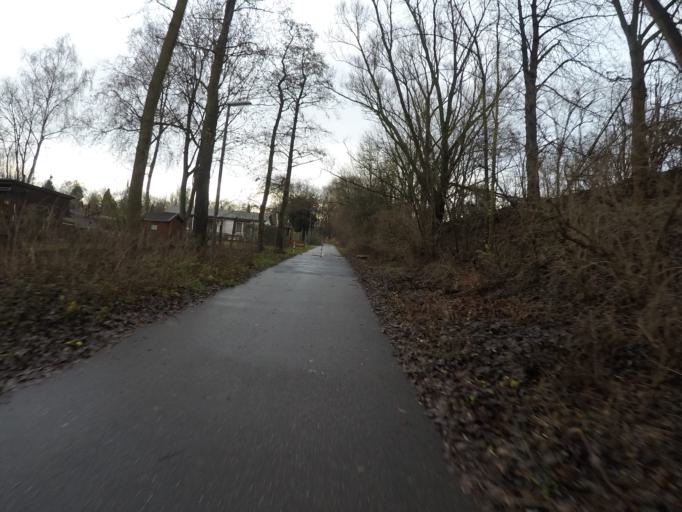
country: DE
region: Hamburg
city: Kleiner Grasbrook
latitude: 53.5179
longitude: 10.0133
